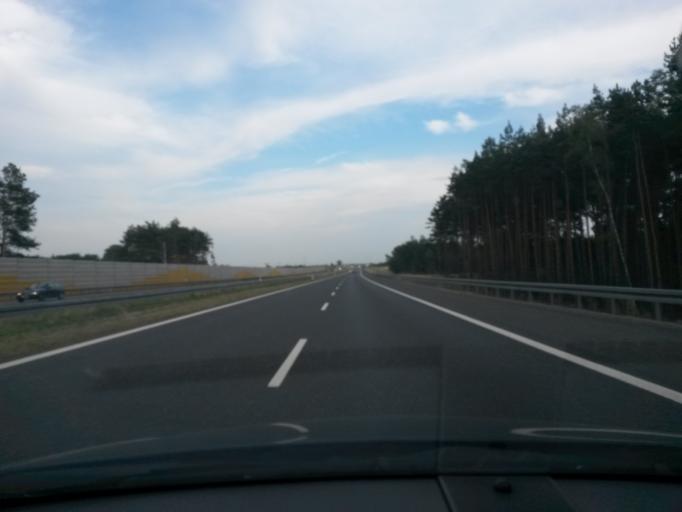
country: PL
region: Lodz Voivodeship
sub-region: Powiat leczycki
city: Swinice Warckie
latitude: 52.0247
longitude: 18.9198
